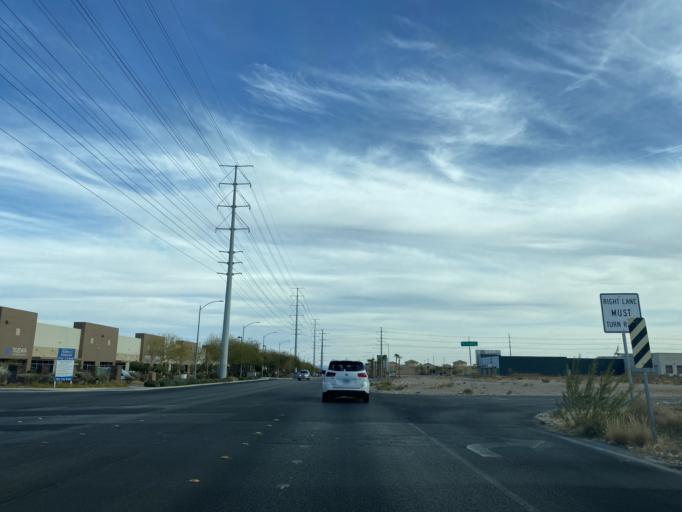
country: US
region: Nevada
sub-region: Clark County
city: Enterprise
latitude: 36.0557
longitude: -115.2479
